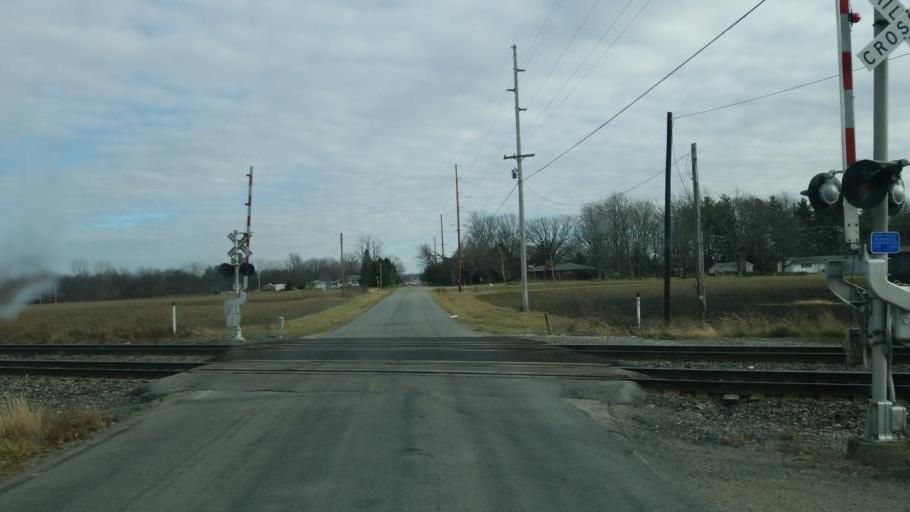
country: US
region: Ohio
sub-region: Crawford County
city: Crestline
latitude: 40.7697
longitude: -82.7475
